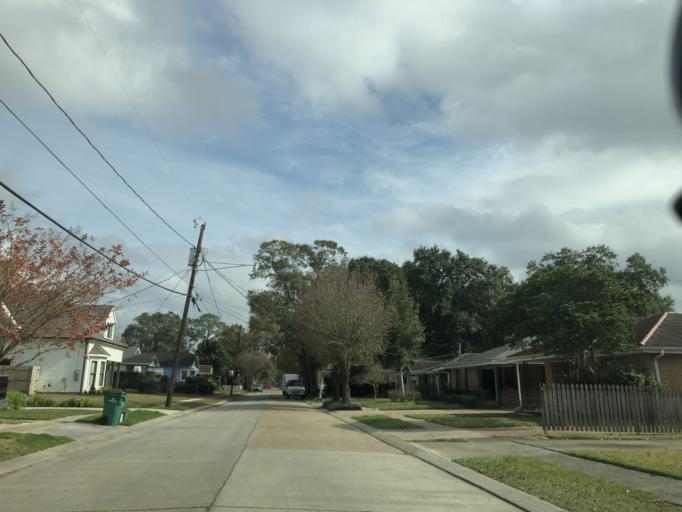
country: US
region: Louisiana
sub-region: Jefferson Parish
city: Metairie Terrace
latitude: 29.9776
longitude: -90.1669
